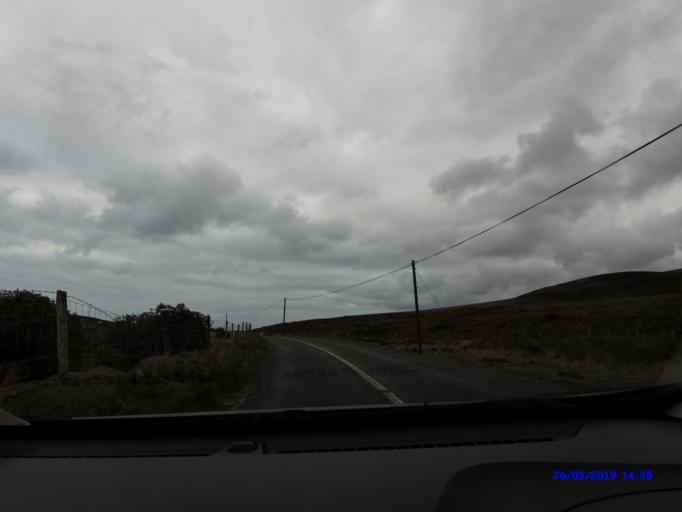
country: IE
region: Connaught
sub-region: Maigh Eo
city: Crossmolina
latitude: 54.2979
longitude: -9.5411
